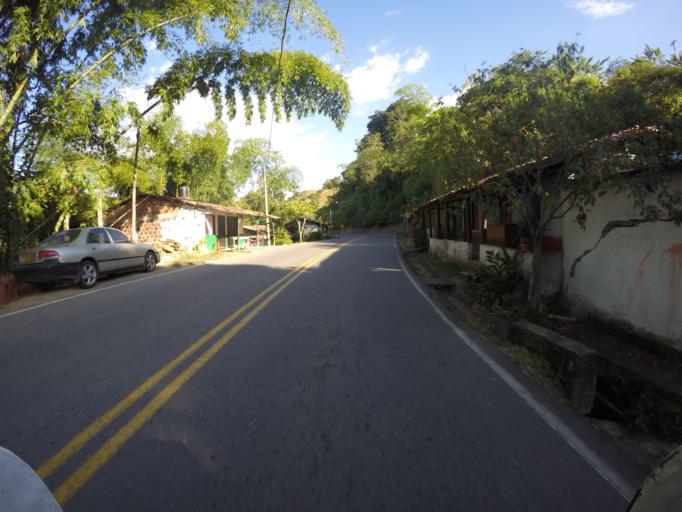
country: CO
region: Valle del Cauca
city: Cartago
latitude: 4.7099
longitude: -75.8578
